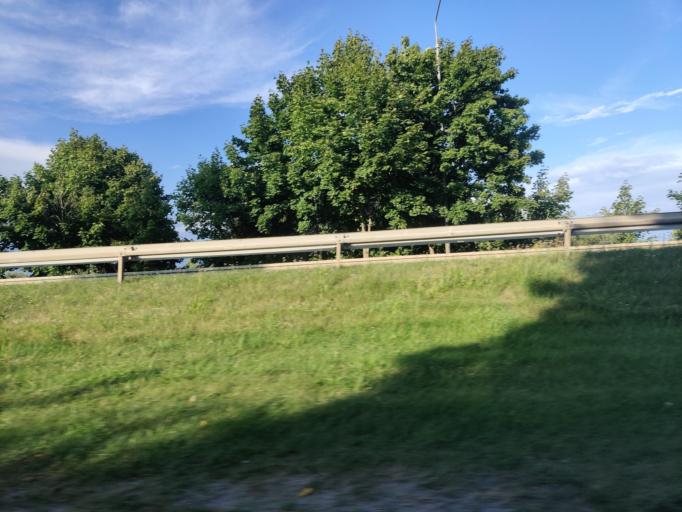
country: PL
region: Greater Poland Voivodeship
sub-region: Konin
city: Konin
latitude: 52.2073
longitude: 18.2660
